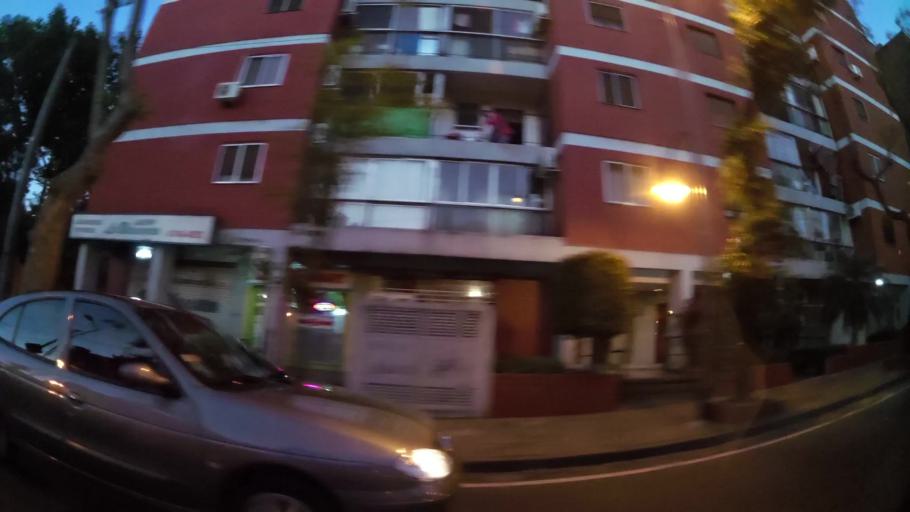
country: AR
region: Buenos Aires
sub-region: Partido de Tigre
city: Tigre
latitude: -34.4364
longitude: -58.5610
